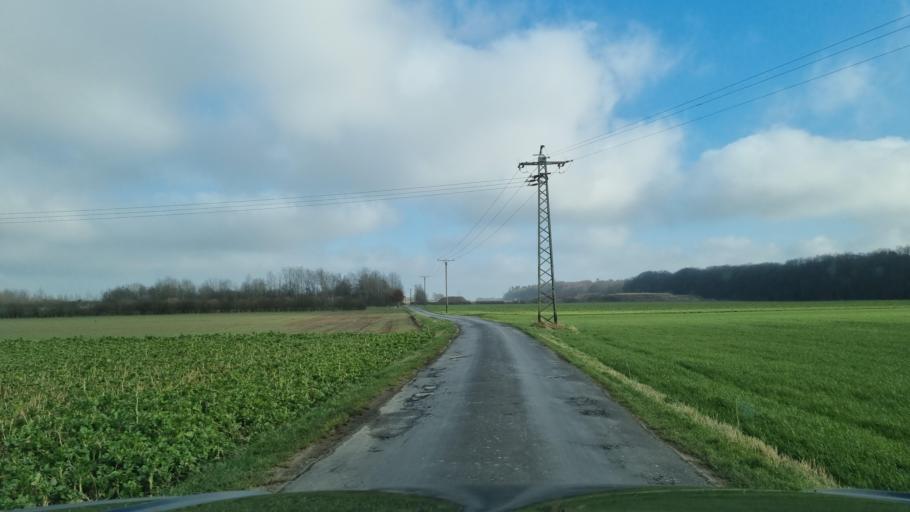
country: DE
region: North Rhine-Westphalia
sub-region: Regierungsbezirk Dusseldorf
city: Kleve
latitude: 51.7443
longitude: 6.1718
